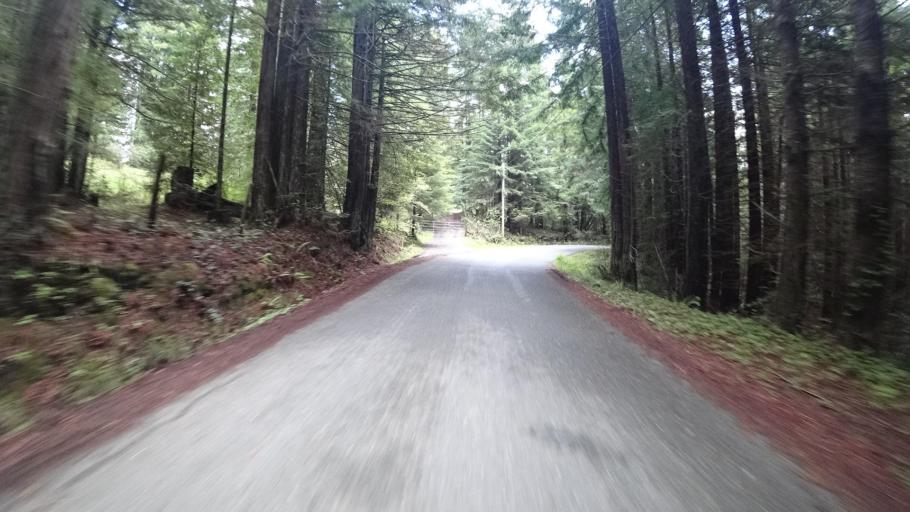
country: US
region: California
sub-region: Humboldt County
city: Blue Lake
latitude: 40.8509
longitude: -123.9281
